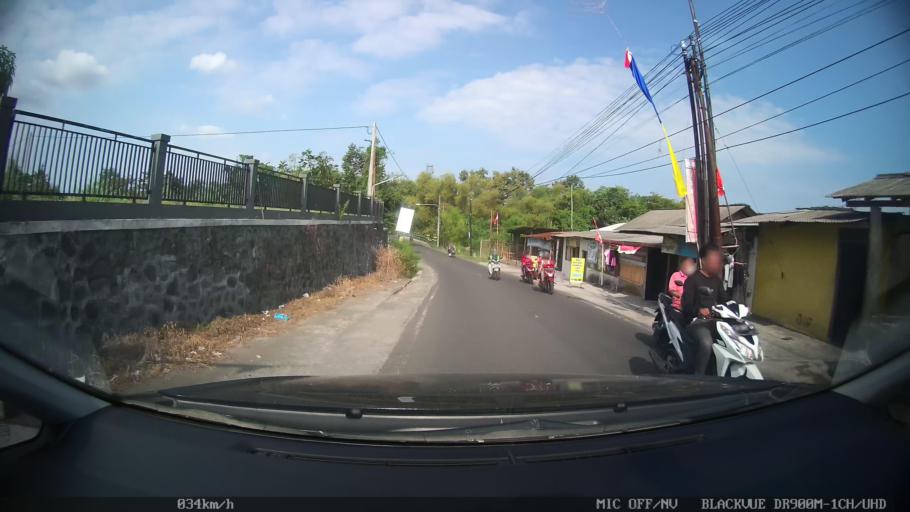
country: ID
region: Daerah Istimewa Yogyakarta
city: Depok
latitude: -7.7539
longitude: 110.4459
